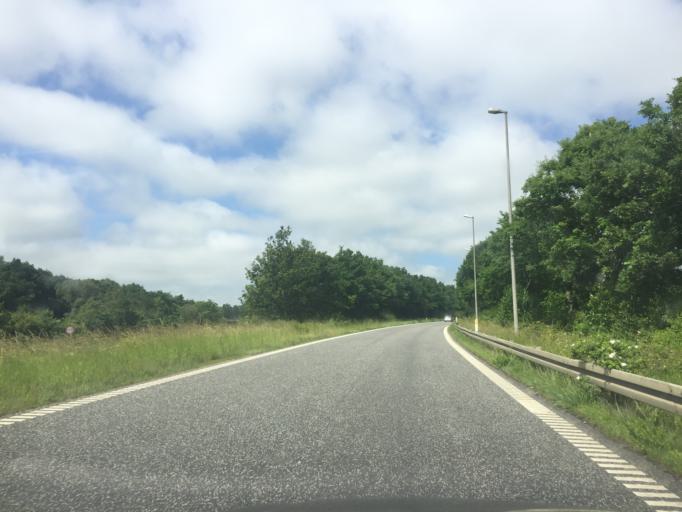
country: DK
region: Capital Region
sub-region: Hoje-Taastrup Kommune
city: Taastrup
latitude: 55.6650
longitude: 12.2854
